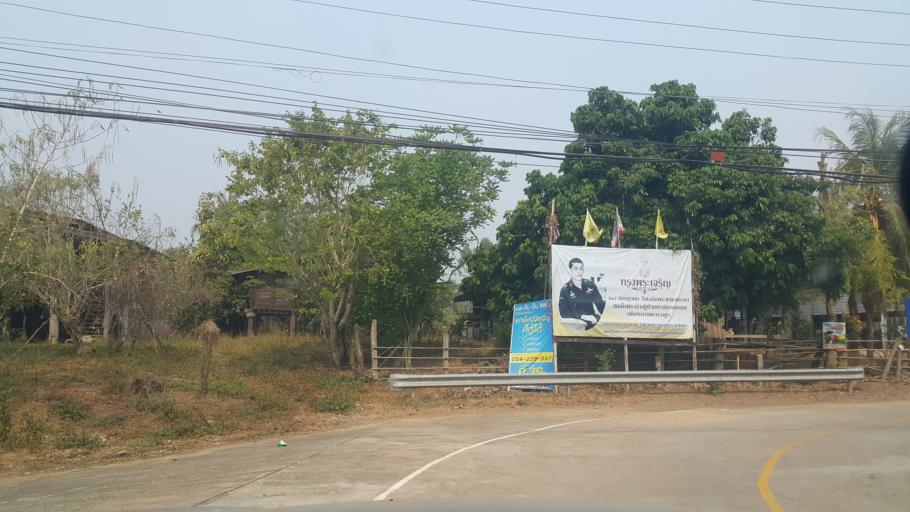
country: TH
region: Lampang
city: Thoen
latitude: 17.7520
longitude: 99.2302
